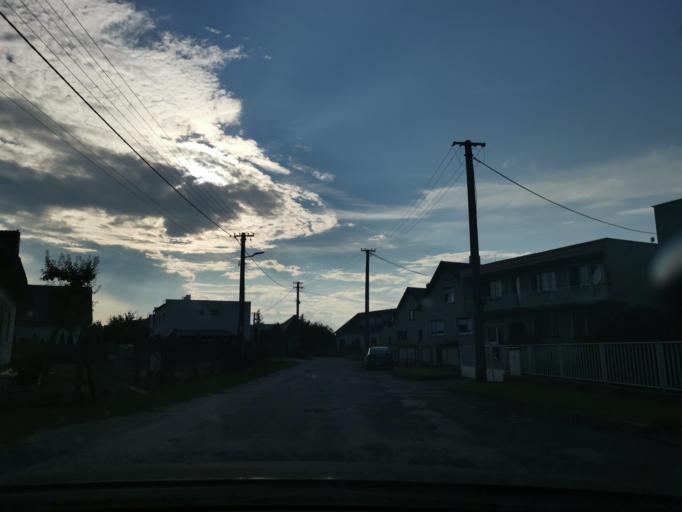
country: SK
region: Trnavsky
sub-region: Okres Senica
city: Senica
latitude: 48.6577
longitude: 17.2623
